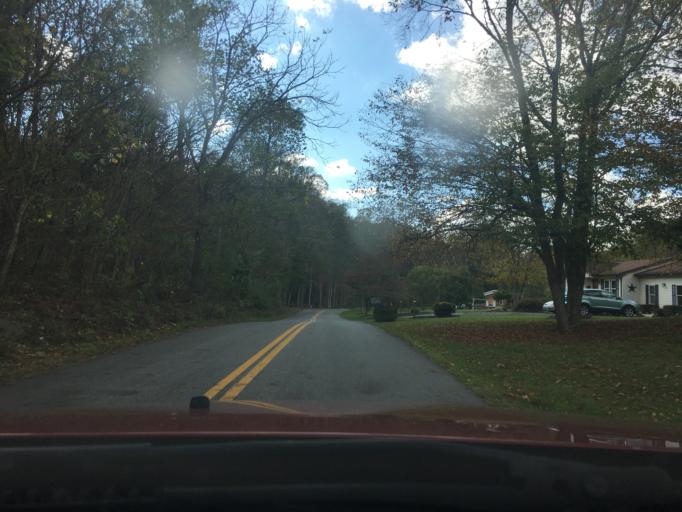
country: US
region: Virginia
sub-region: Giles County
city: Pembroke
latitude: 37.3407
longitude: -80.6238
